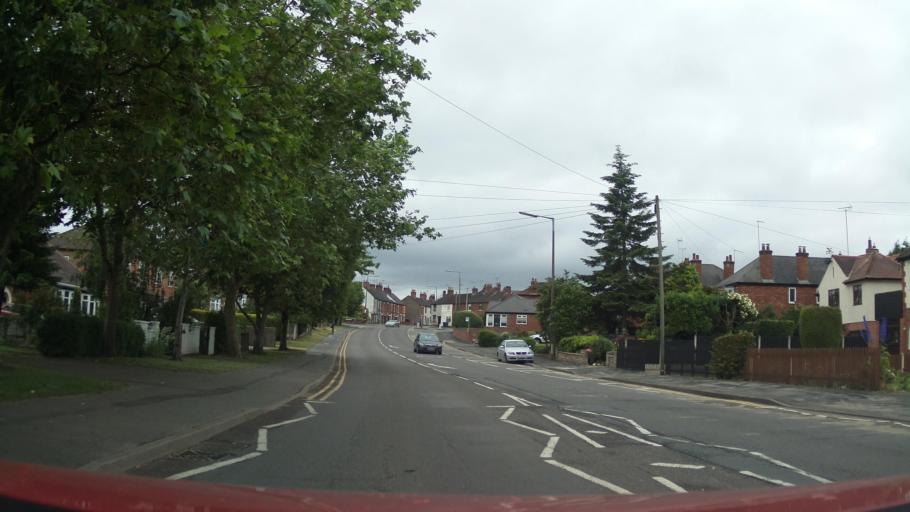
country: GB
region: England
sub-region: Staffordshire
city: Burton upon Trent
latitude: 52.8270
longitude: -1.6502
